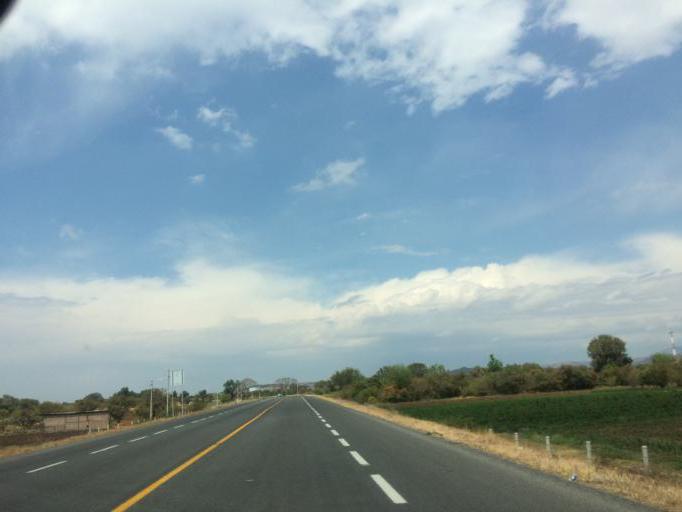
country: MX
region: Guanajuato
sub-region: Silao de la Victoria
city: Loma de Yerbabuena
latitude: 21.0256
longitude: -101.4437
